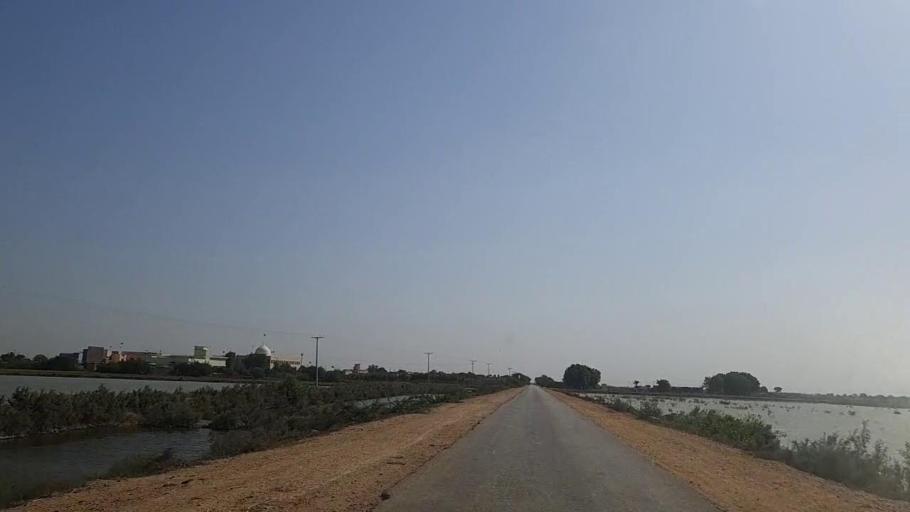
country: PK
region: Sindh
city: Mirpur Batoro
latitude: 24.6434
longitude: 68.2902
